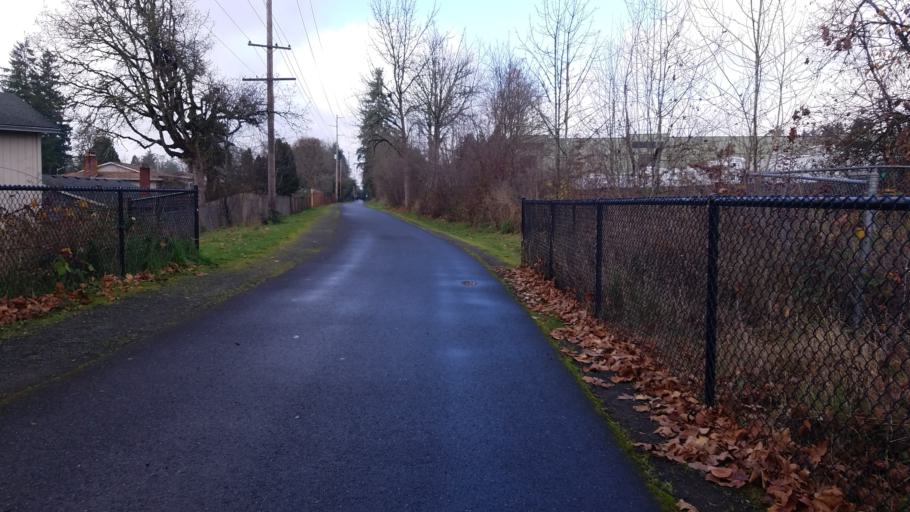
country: US
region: Oregon
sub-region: Clackamas County
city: Jennings Lodge
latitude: 45.4005
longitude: -122.6265
